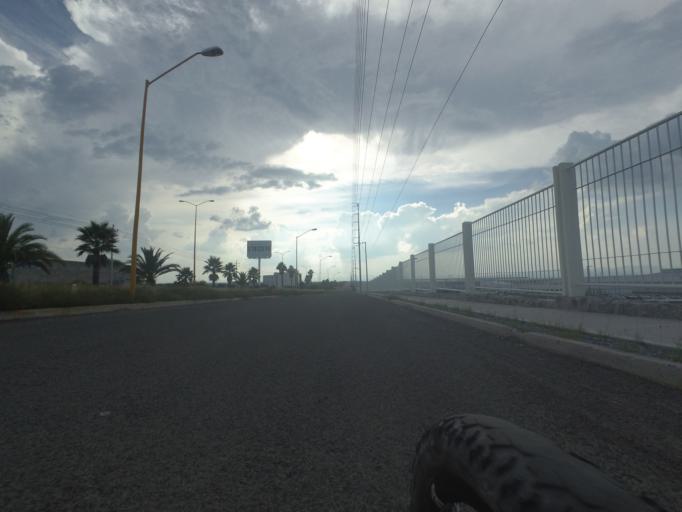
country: MX
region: Aguascalientes
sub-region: Aguascalientes
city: Penuelas (El Cienegal)
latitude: 21.7248
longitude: -102.2893
